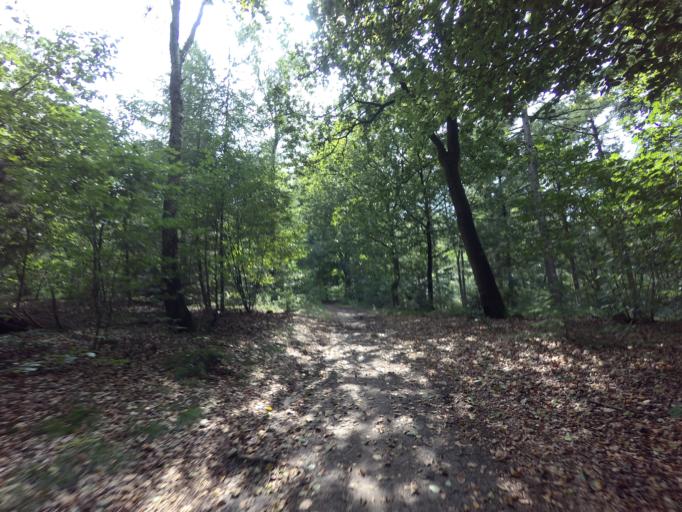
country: NL
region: Gelderland
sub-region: Gemeente Ede
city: Lunteren
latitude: 52.0815
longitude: 5.6522
